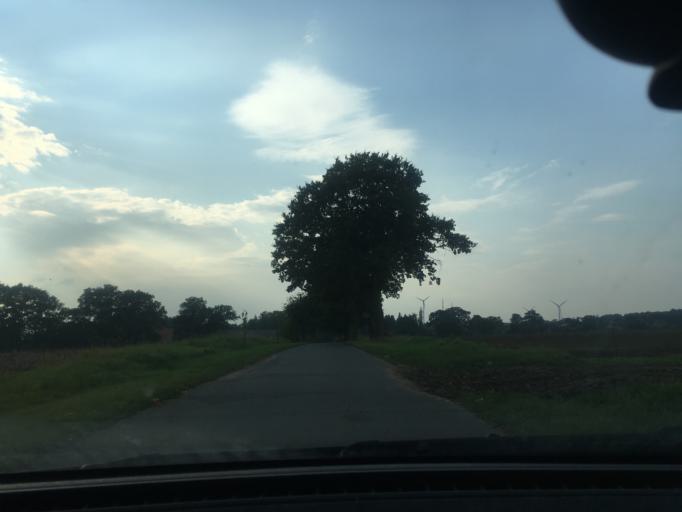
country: DE
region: Lower Saxony
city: Vastorf
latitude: 53.2054
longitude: 10.5515
